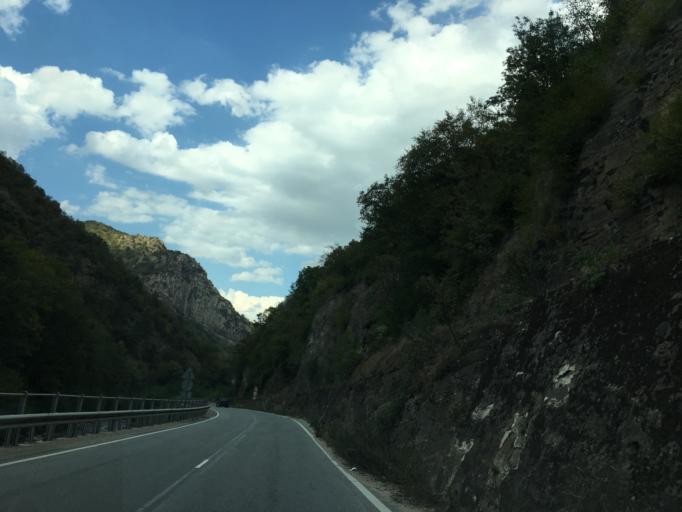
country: BG
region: Pazardzhik
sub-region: Obshtina Septemvri
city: Septemvri
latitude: 42.1031
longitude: 24.1024
